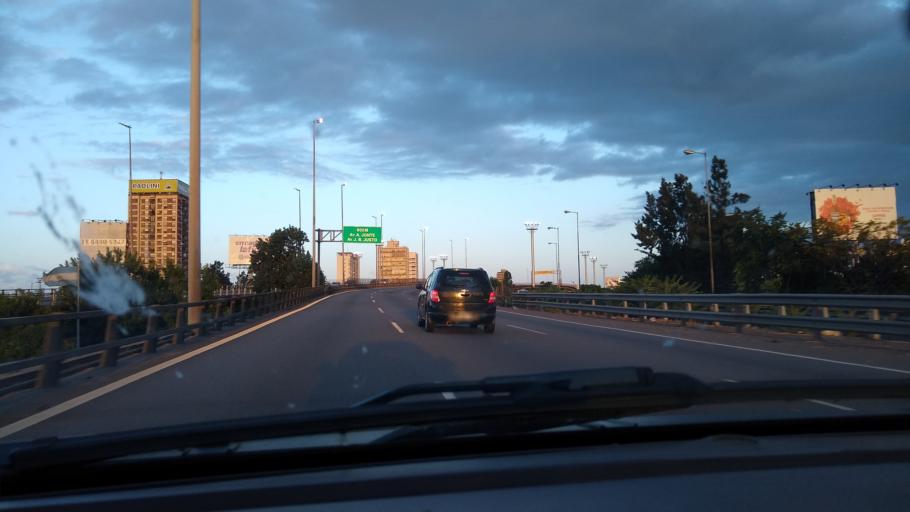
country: AR
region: Buenos Aires
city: Caseros
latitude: -34.6350
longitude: -58.5341
